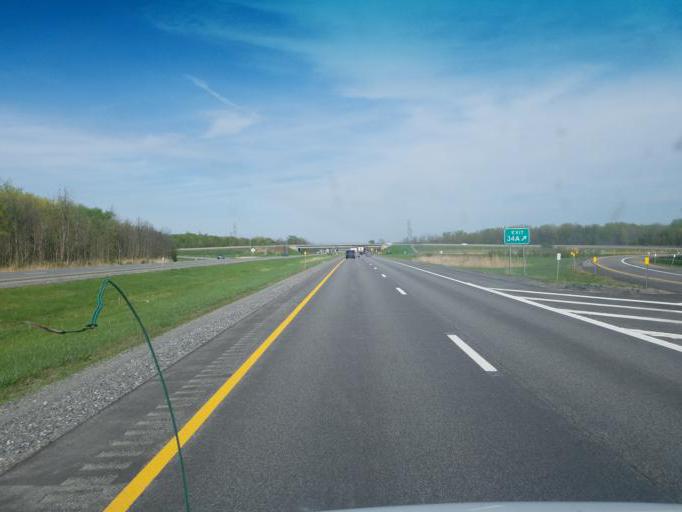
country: US
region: New York
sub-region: Onondaga County
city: East Syracuse
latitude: 43.0945
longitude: -76.0485
